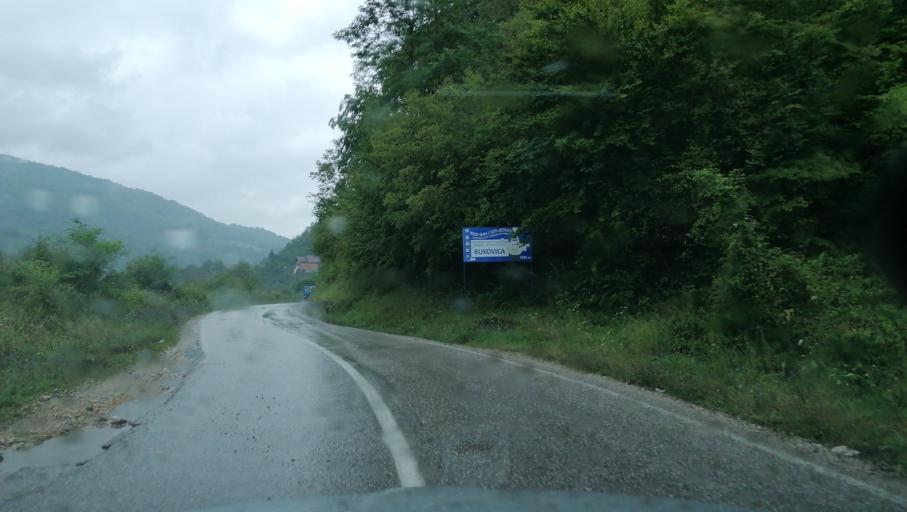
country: BA
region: Republika Srpska
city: Foca
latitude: 43.4826
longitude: 18.7446
